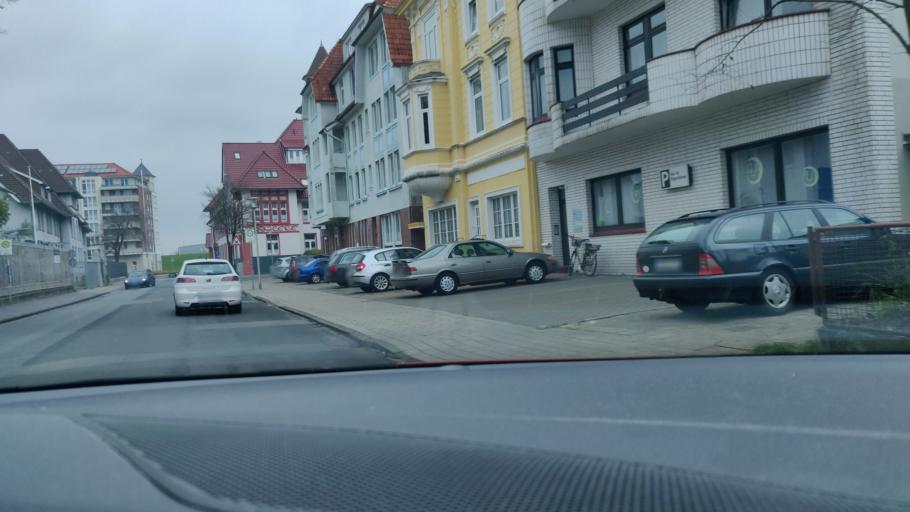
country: DE
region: Lower Saxony
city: Cuxhaven
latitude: 53.8721
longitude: 8.6980
